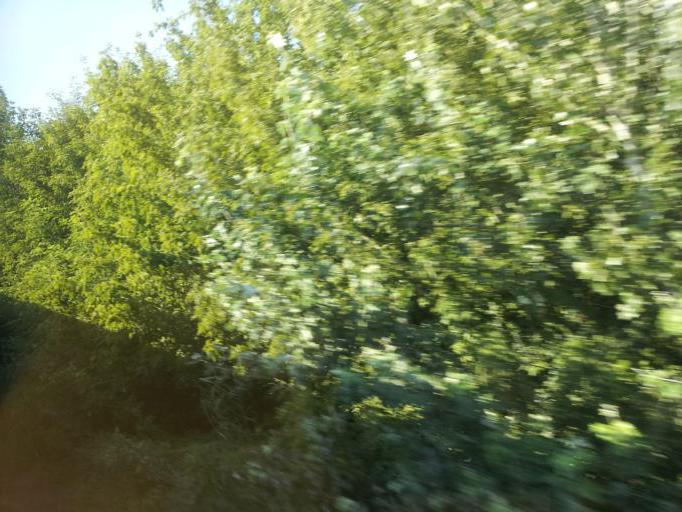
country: HU
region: Budapest
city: Budapest XX. keruelet
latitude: 47.4177
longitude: 19.1073
